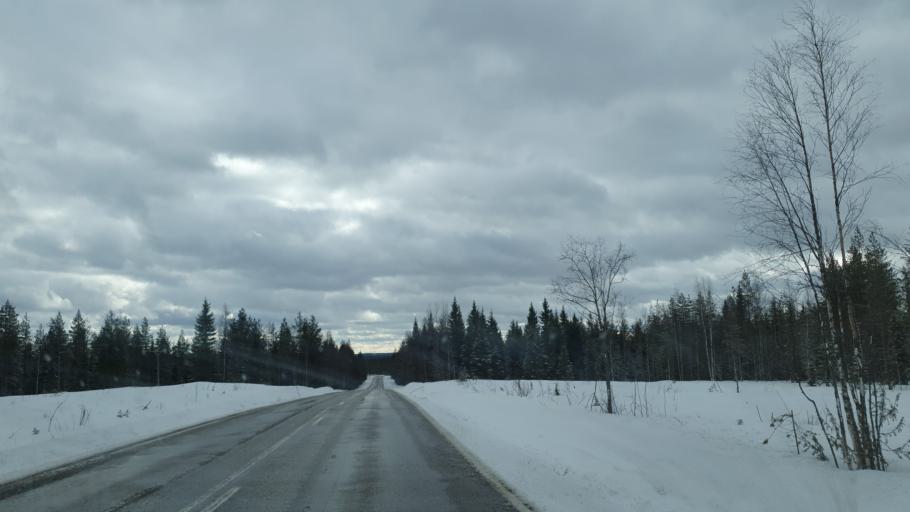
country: FI
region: Kainuu
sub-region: Kehys-Kainuu
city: Puolanka
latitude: 65.0771
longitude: 27.6989
